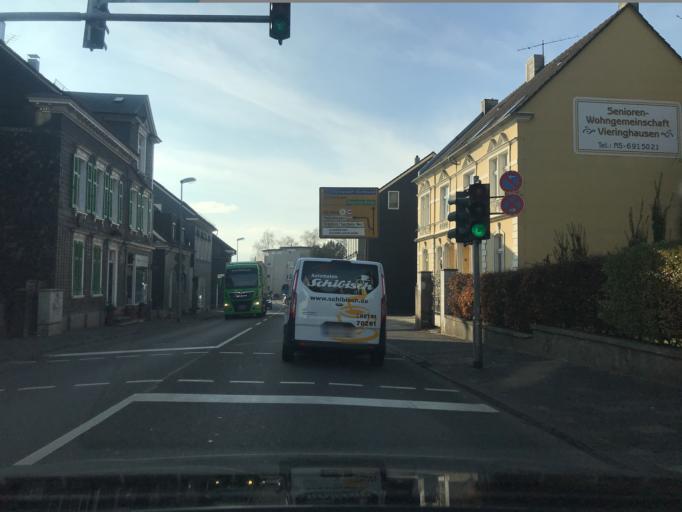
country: DE
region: North Rhine-Westphalia
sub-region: Regierungsbezirk Dusseldorf
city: Remscheid
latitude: 51.1769
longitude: 7.1649
